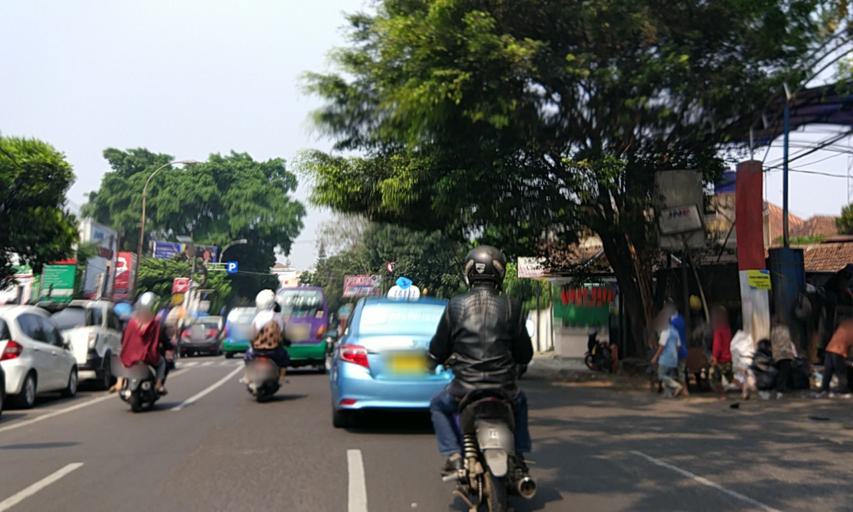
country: ID
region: West Java
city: Bandung
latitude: -6.9101
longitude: 107.6042
